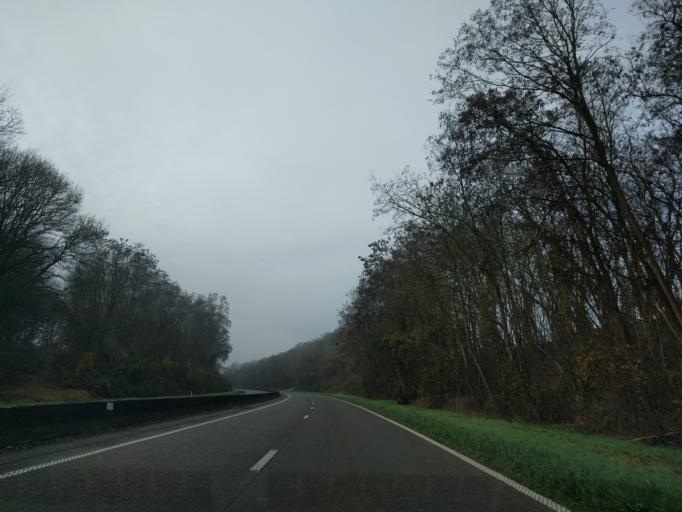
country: BE
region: Wallonia
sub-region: Province de Namur
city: Dinant
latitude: 50.2447
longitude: 4.9001
